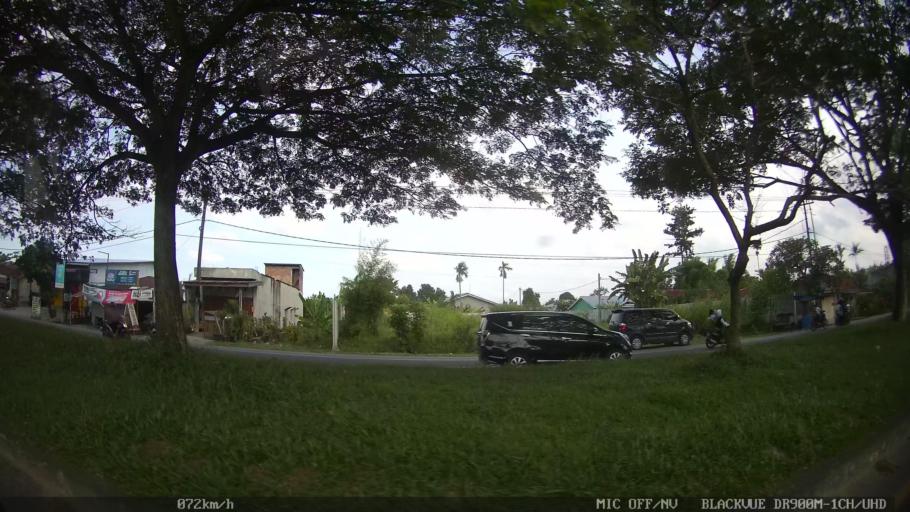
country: ID
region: North Sumatra
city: Percut
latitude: 3.5685
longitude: 98.7962
